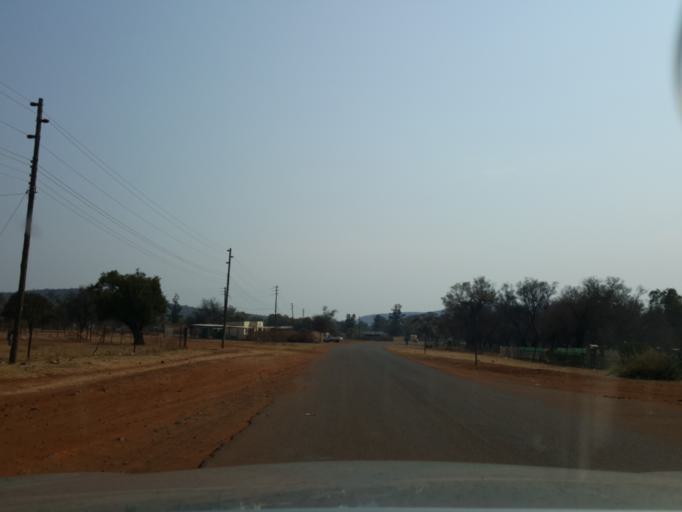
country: BW
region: South East
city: Lobatse
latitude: -25.3167
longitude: 25.7965
